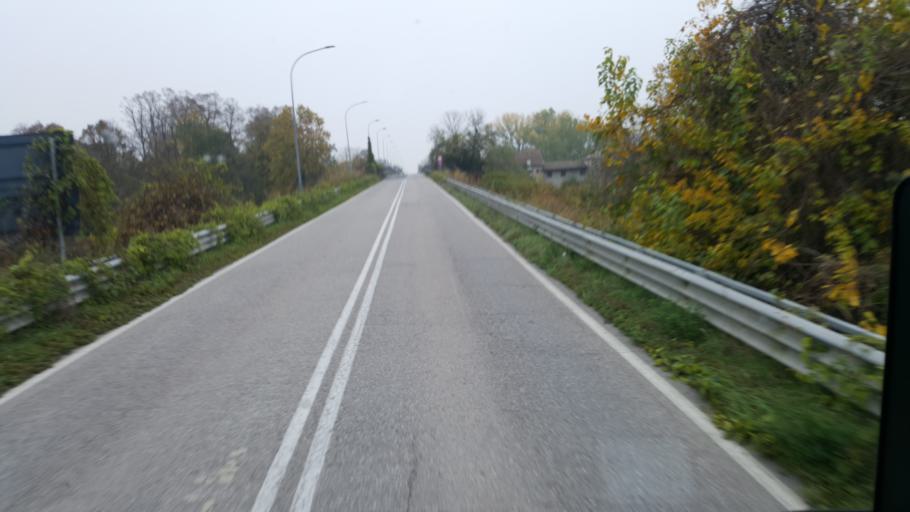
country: IT
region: Veneto
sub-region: Provincia di Rovigo
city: Ficarolo
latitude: 44.9457
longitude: 11.4200
